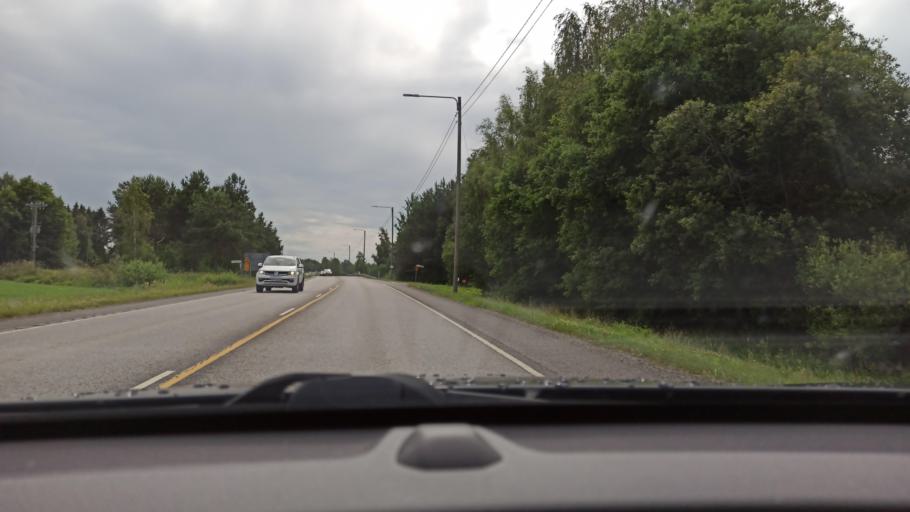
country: FI
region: Satakunta
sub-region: Pori
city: Pori
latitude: 61.5034
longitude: 21.7492
